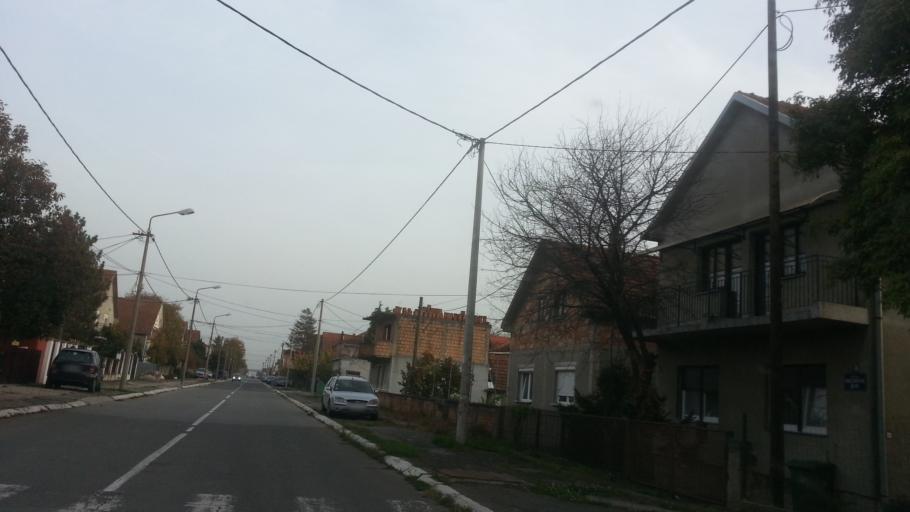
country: RS
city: Novi Banovci
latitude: 44.8954
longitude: 20.2819
